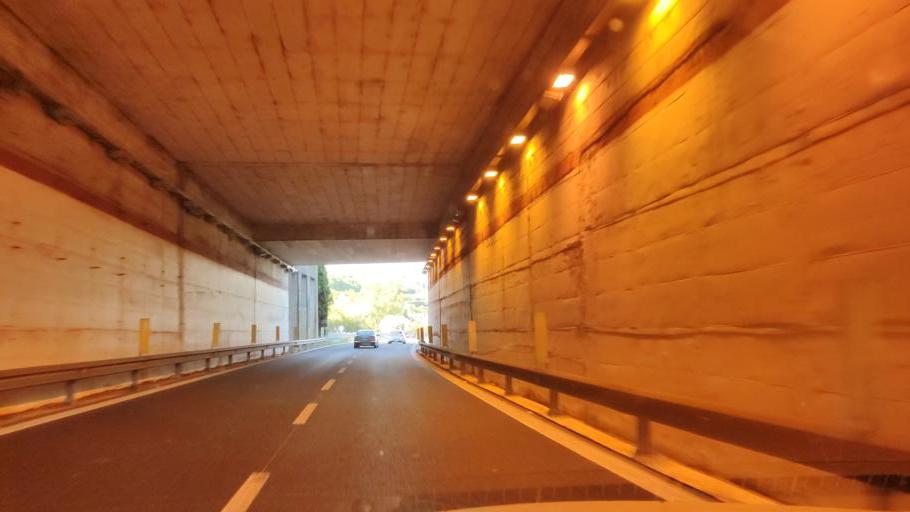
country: IT
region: Latium
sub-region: Provincia di Viterbo
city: Orte Scalo
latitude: 42.4603
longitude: 12.4126
